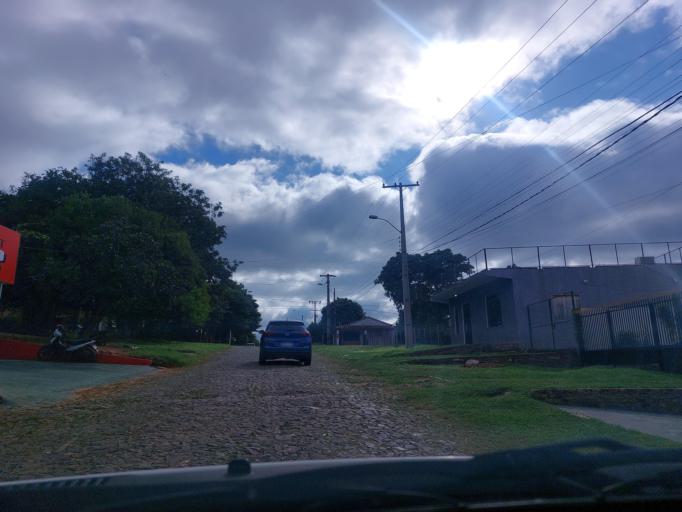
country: PY
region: San Pedro
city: Guayaybi
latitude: -24.6711
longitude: -56.4398
